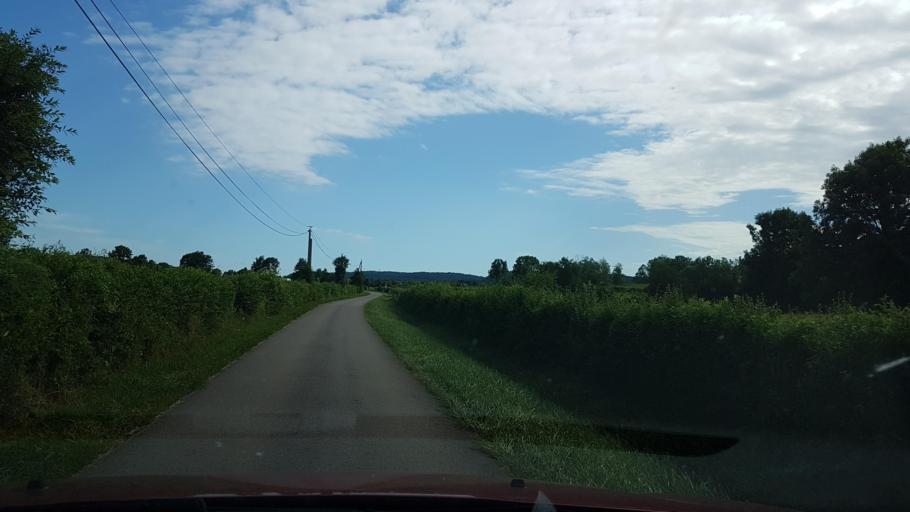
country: FR
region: Franche-Comte
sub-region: Departement du Jura
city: Clairvaux-les-Lacs
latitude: 46.5867
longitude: 5.7286
